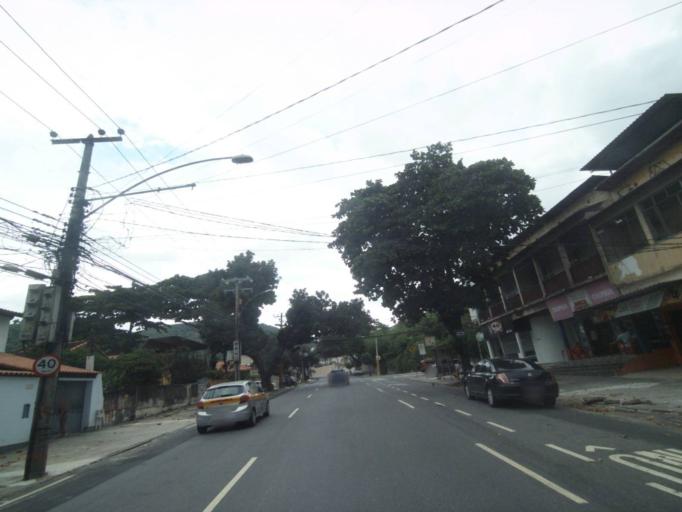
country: BR
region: Rio de Janeiro
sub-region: Nilopolis
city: Nilopolis
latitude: -22.8877
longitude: -43.3943
